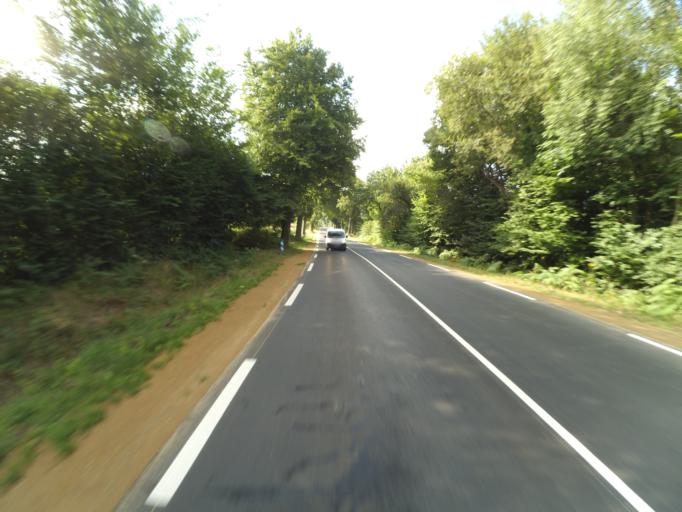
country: FR
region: Brittany
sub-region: Departement du Finistere
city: Redene
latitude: 47.8332
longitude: -3.5008
